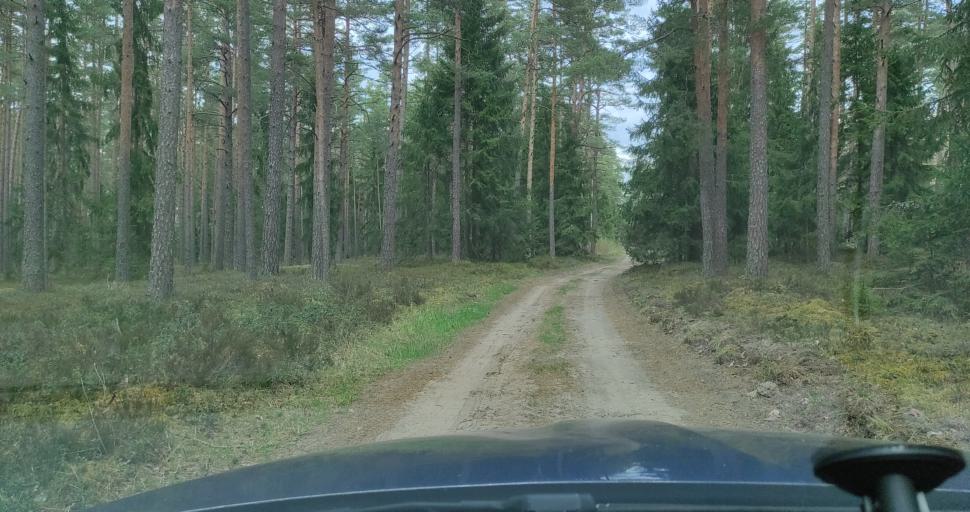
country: LV
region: Talsu Rajons
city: Stende
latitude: 57.2179
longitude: 22.2467
